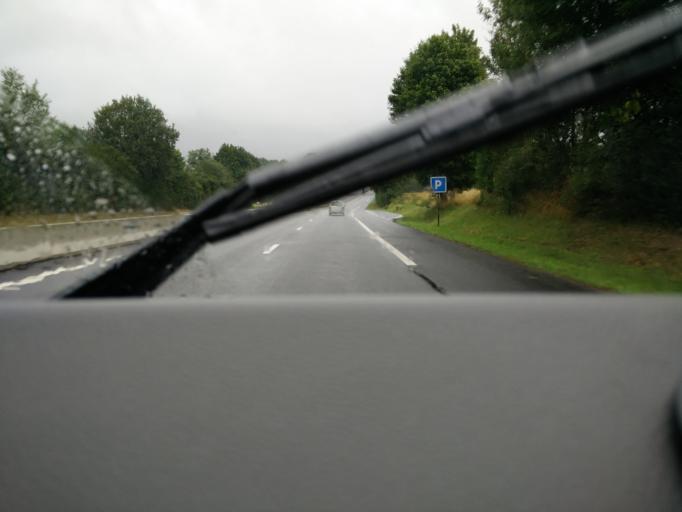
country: FR
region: Nord-Pas-de-Calais
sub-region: Departement du Pas-de-Calais
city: Saint-Pol-sur-Ternoise
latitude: 50.3678
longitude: 2.3662
